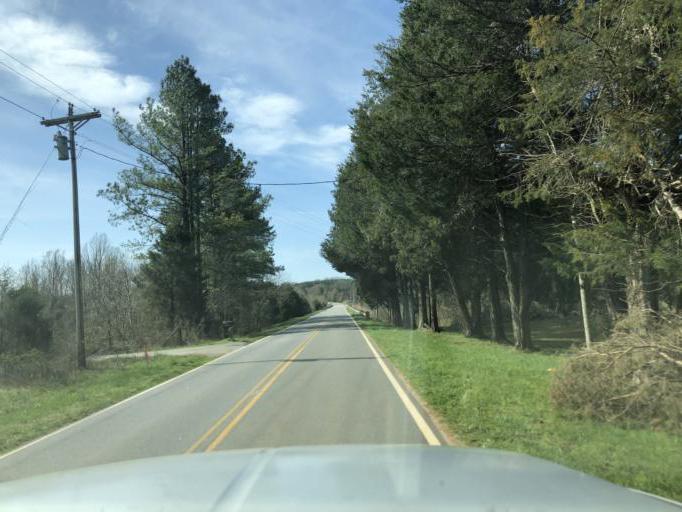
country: US
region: North Carolina
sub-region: Cleveland County
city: Shelby
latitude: 35.4508
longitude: -81.6420
